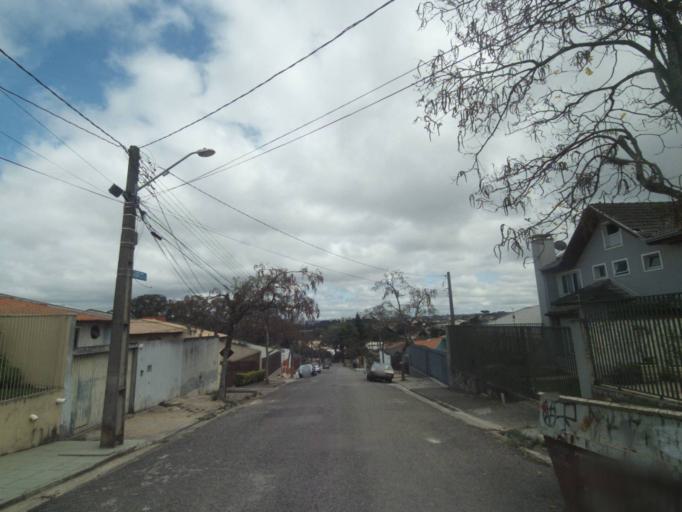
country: BR
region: Parana
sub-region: Pinhais
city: Pinhais
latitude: -25.3965
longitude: -49.2145
